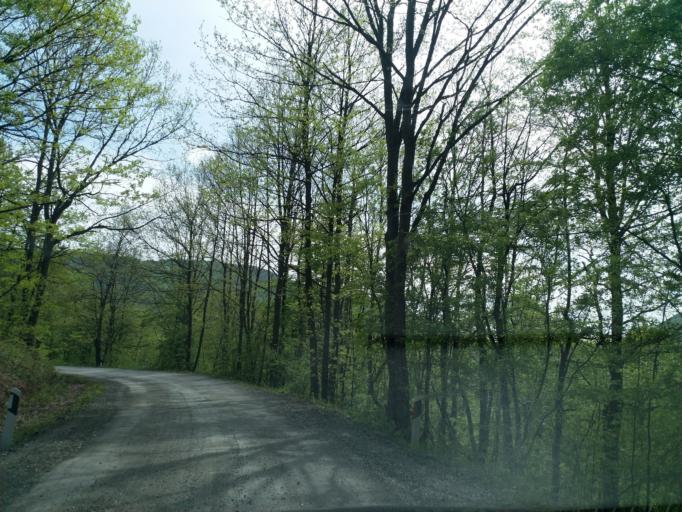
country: RS
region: Central Serbia
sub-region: Pomoravski Okrug
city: Despotovac
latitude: 43.9649
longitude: 21.5581
